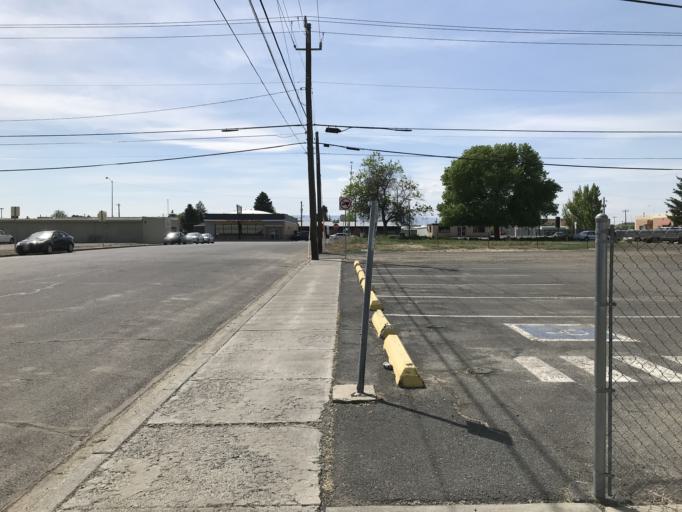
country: US
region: Washington
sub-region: Grant County
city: Quincy
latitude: 47.2308
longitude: -119.8521
